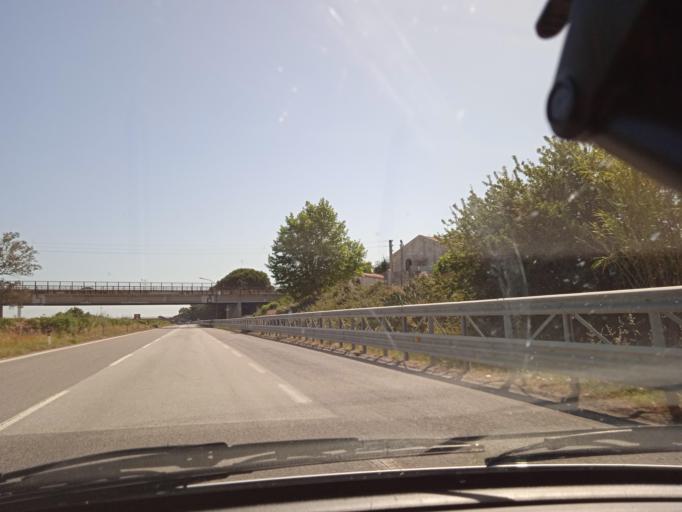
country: IT
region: Sicily
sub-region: Messina
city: Meri
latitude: 38.1827
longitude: 15.2548
